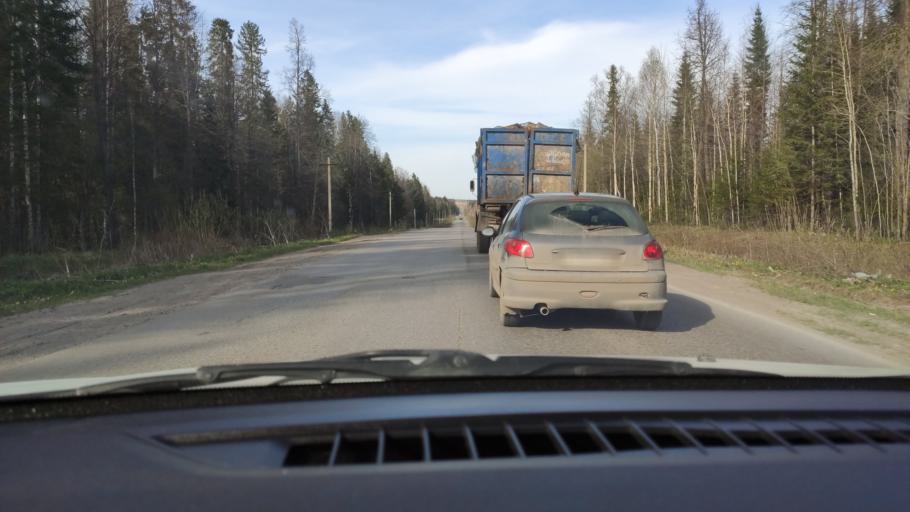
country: RU
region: Perm
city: Novyye Lyady
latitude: 57.9417
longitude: 56.4966
